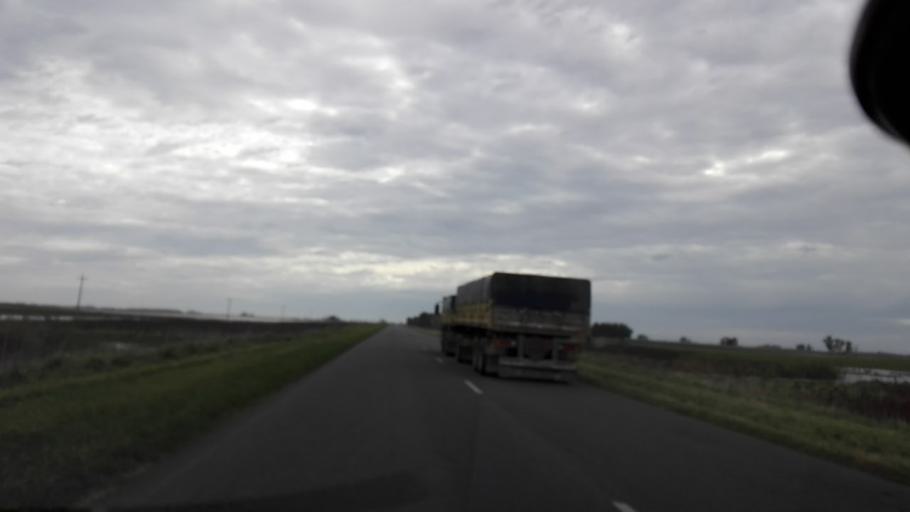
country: AR
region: Buenos Aires
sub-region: Partido de Las Flores
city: Las Flores
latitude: -36.3418
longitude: -59.0151
